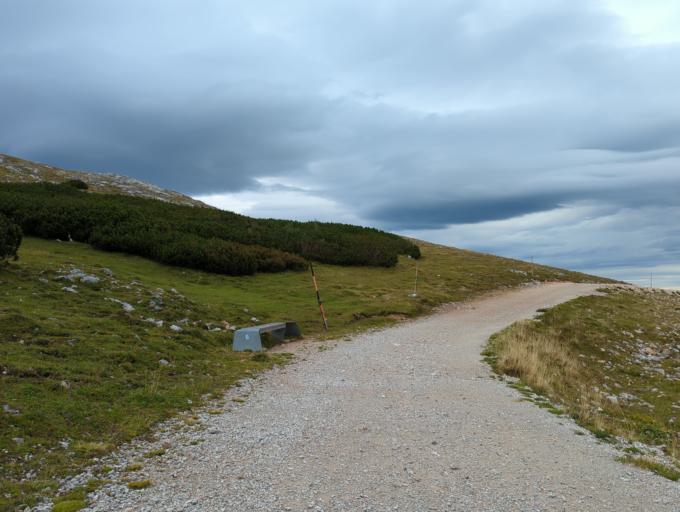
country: AT
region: Lower Austria
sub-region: Politischer Bezirk Neunkirchen
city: Reichenau an der Rax
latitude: 47.7586
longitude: 15.8288
